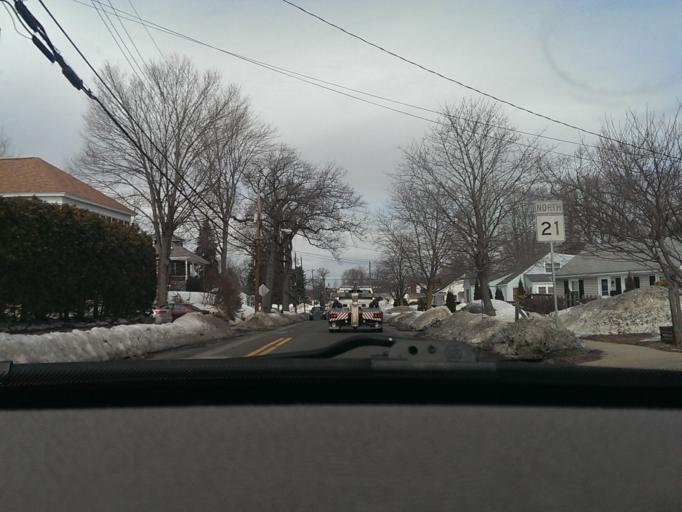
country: US
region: Massachusetts
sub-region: Hampden County
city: Ludlow
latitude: 42.1625
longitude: -72.4804
